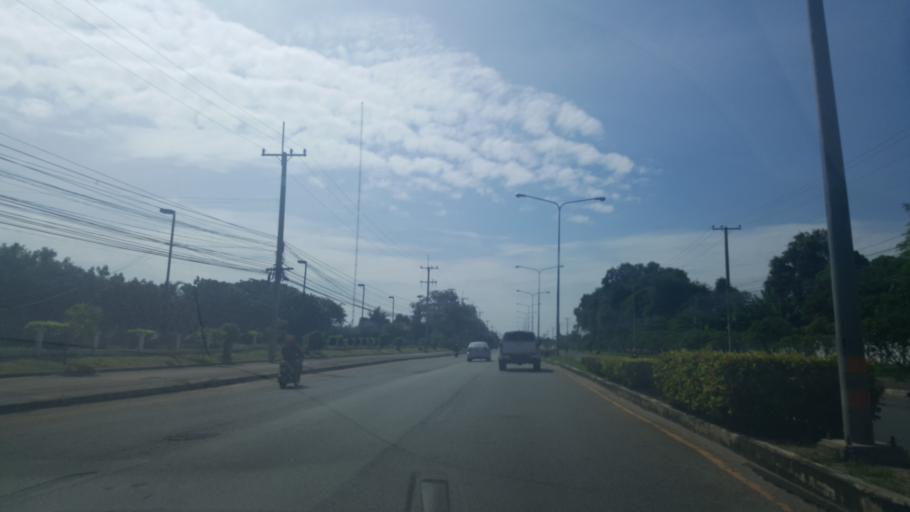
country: TH
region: Chon Buri
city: Sattahip
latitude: 12.6700
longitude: 100.8958
